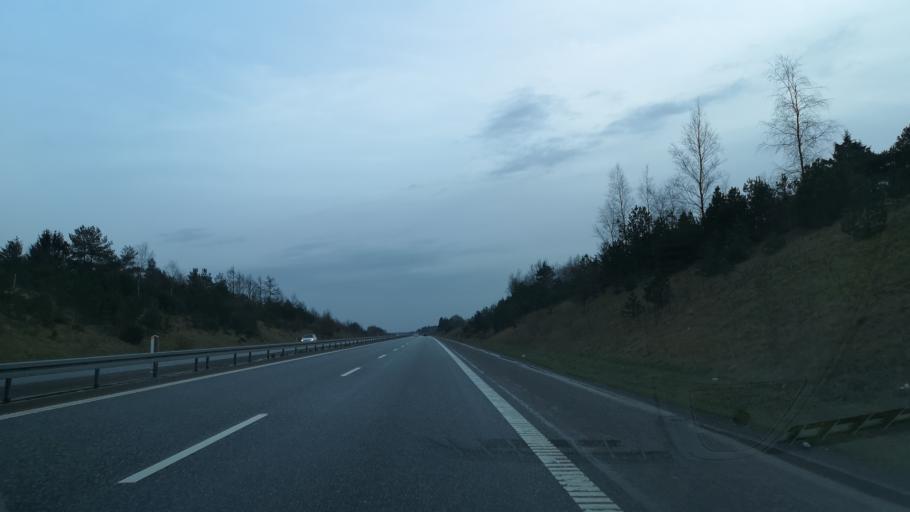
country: DK
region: Central Jutland
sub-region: Herning Kommune
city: Lind
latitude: 56.0690
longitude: 8.9970
